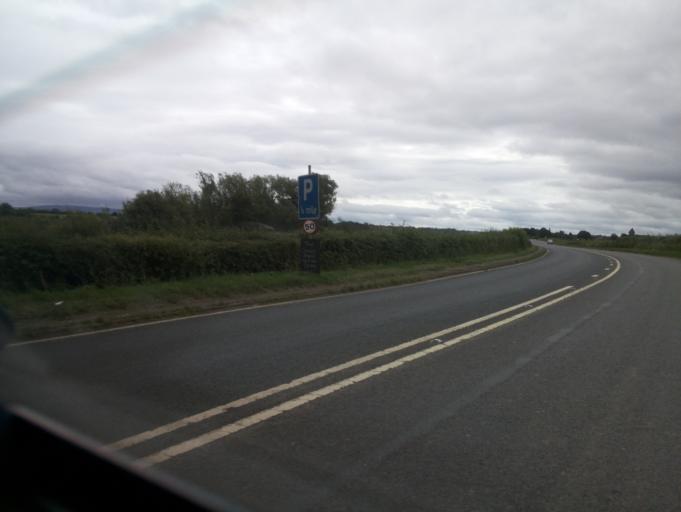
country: GB
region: England
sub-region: Worcestershire
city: Kempsey
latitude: 52.1210
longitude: -2.2238
